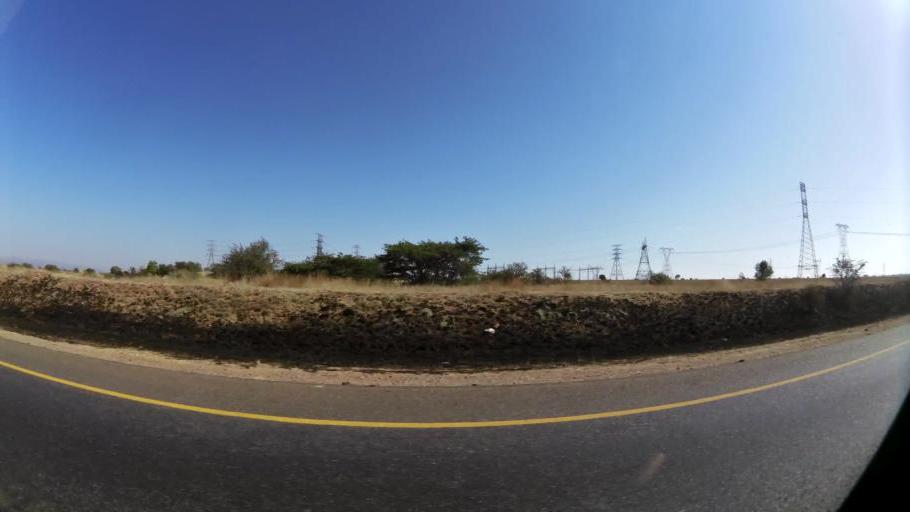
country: ZA
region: Gauteng
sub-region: City of Tshwane Metropolitan Municipality
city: Mabopane
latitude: -25.5630
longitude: 28.1076
